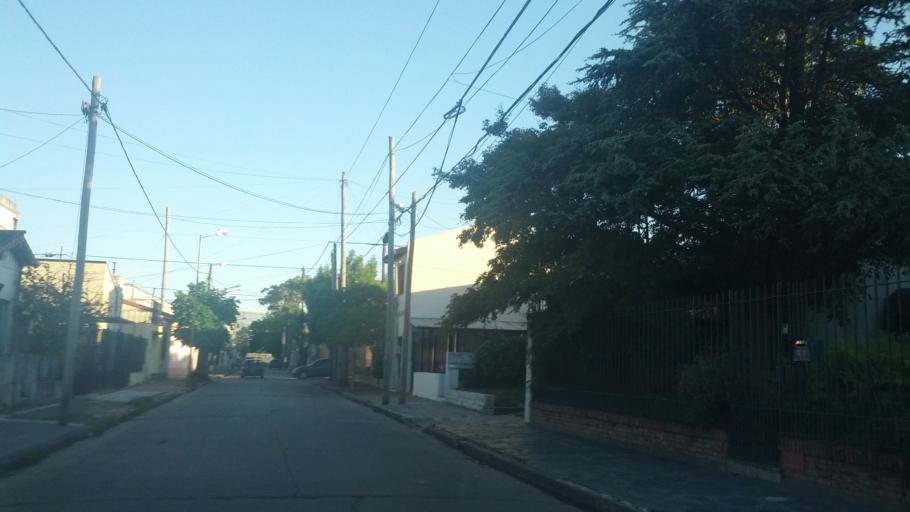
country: AR
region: Buenos Aires
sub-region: Partido de Lomas de Zamora
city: Lomas de Zamora
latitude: -34.7805
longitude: -58.4085
